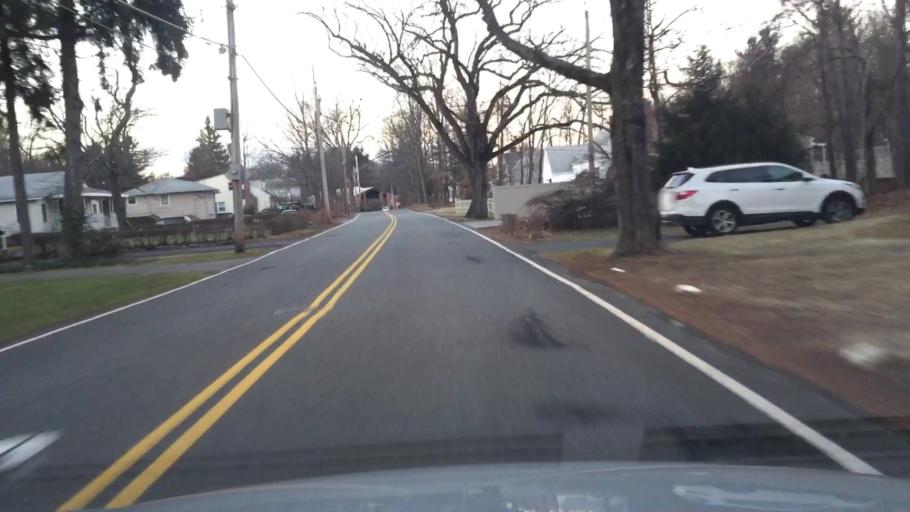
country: US
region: Massachusetts
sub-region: Worcester County
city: West Boylston
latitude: 42.3319
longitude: -71.8185
